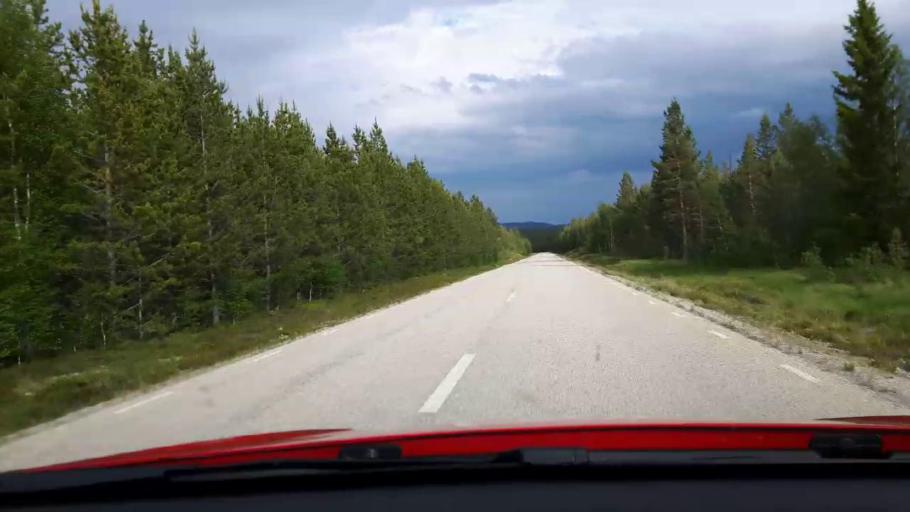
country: SE
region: Jaemtland
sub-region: Bergs Kommun
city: Hoverberg
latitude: 62.6688
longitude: 14.0340
